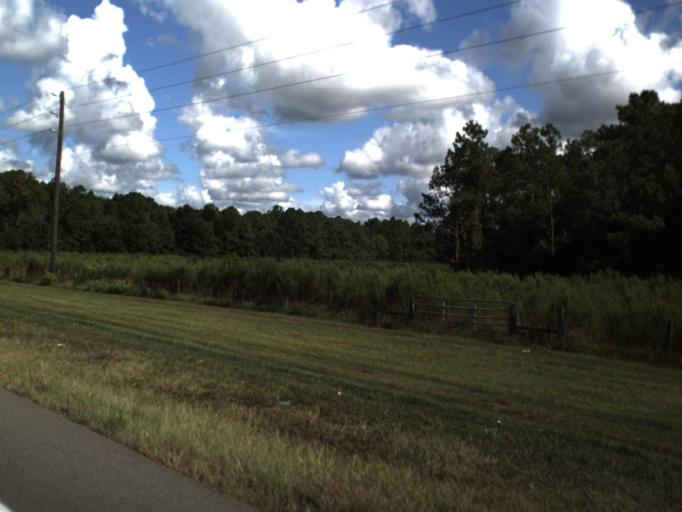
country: US
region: Florida
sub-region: Pasco County
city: Zephyrhills North
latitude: 28.2471
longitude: -82.0539
